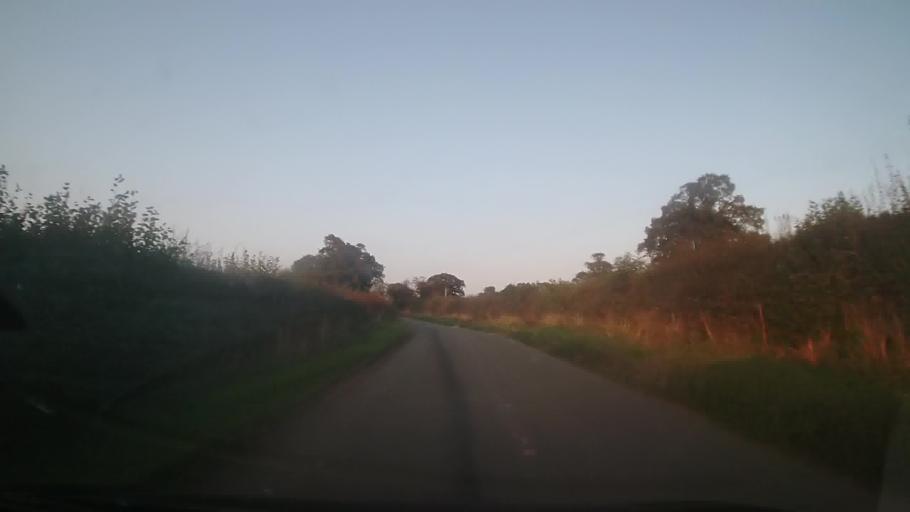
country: GB
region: England
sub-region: Shropshire
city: Bicton
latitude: 52.7714
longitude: -2.7927
